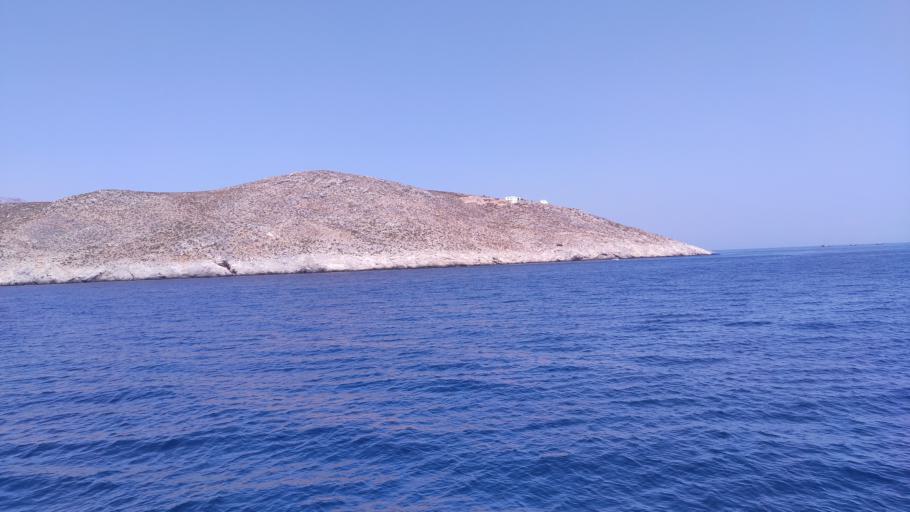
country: GR
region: South Aegean
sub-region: Nomos Dodekanisou
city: Kalymnos
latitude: 36.9408
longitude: 27.0499
